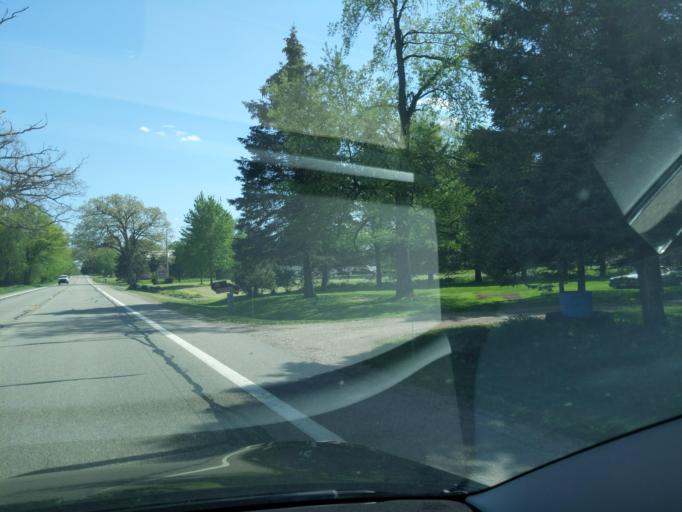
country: US
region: Michigan
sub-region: Kent County
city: Lowell
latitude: 42.8413
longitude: -85.3702
